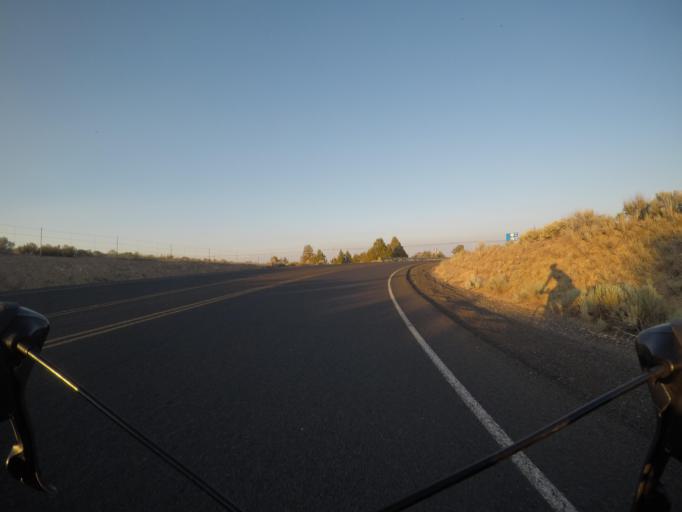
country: US
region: Oregon
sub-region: Deschutes County
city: Redmond
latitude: 44.2767
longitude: -121.2624
